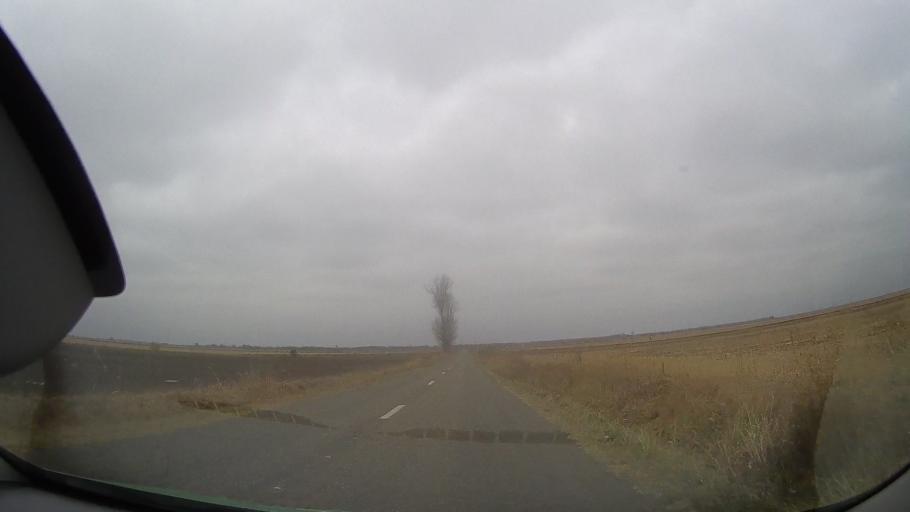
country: RO
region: Buzau
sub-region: Comuna Bradeanu
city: Bradeanu
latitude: 44.9054
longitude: 26.8710
